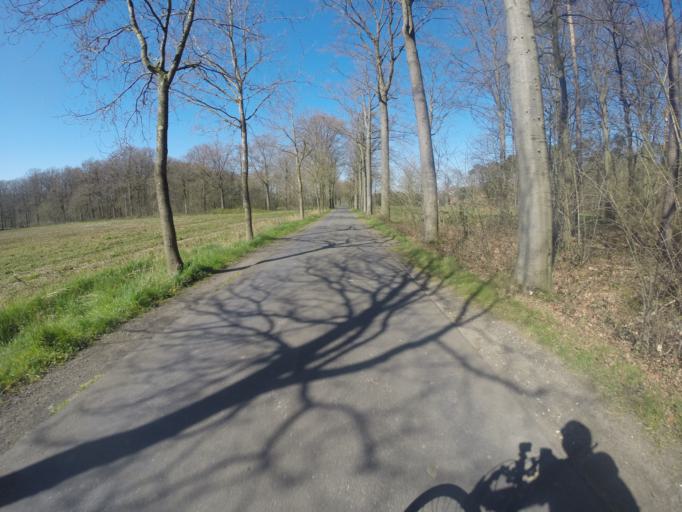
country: BE
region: Flanders
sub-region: Provincie West-Vlaanderen
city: Ruiselede
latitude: 51.0760
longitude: 3.3777
